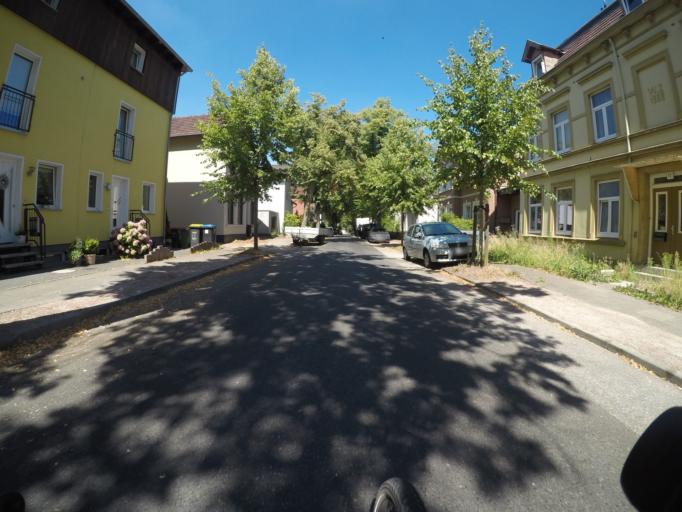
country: DE
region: Hamburg
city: Bergedorf
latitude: 53.4937
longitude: 10.2017
